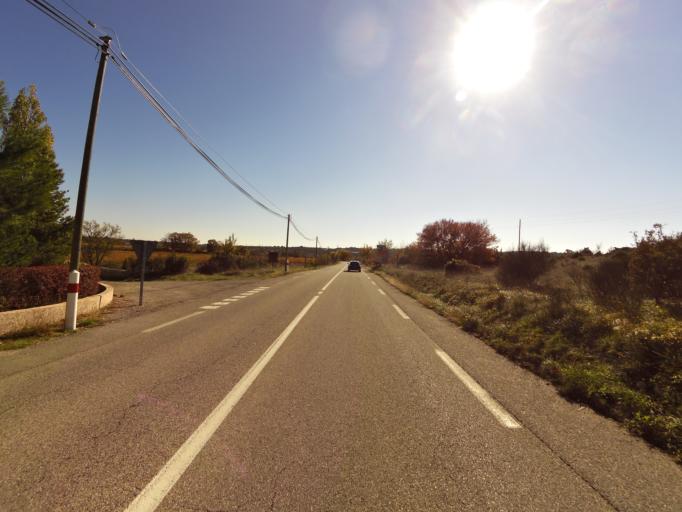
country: FR
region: Languedoc-Roussillon
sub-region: Departement du Gard
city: Saint-Julien-de-Peyrolas
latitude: 44.3906
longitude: 4.5112
